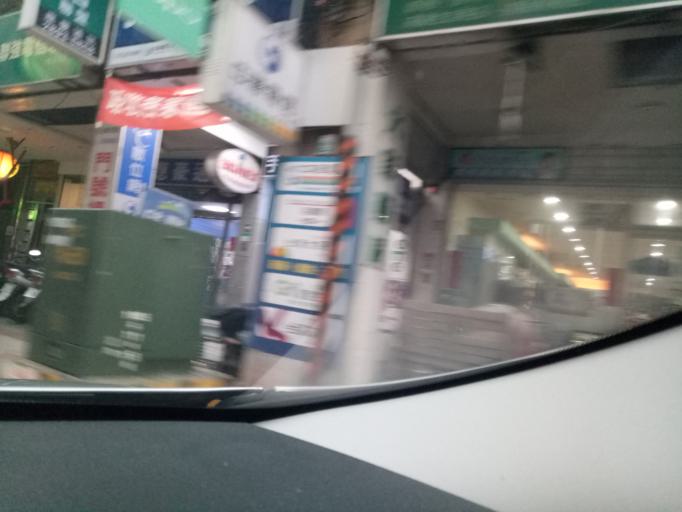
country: TW
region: Taipei
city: Taipei
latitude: 25.1357
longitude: 121.5030
